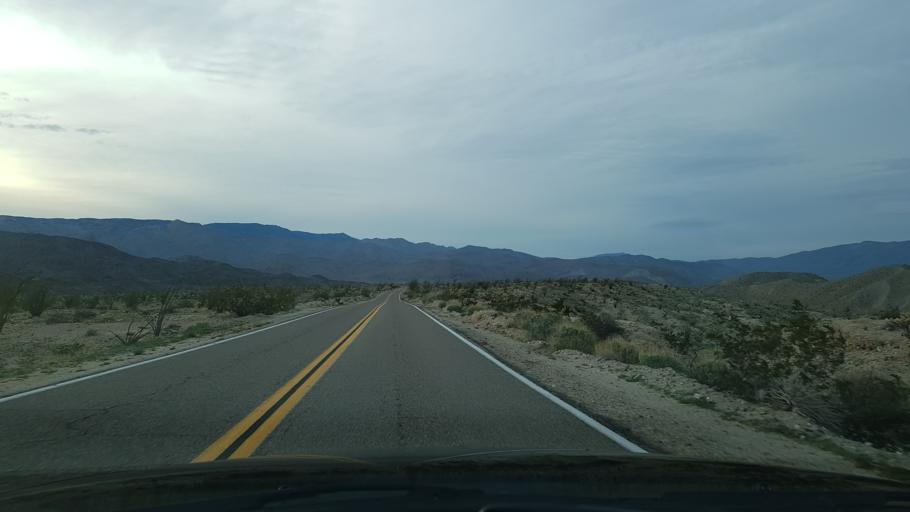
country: MX
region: Baja California
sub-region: Tecate
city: Cereso del Hongo
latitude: 32.8222
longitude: -116.1570
